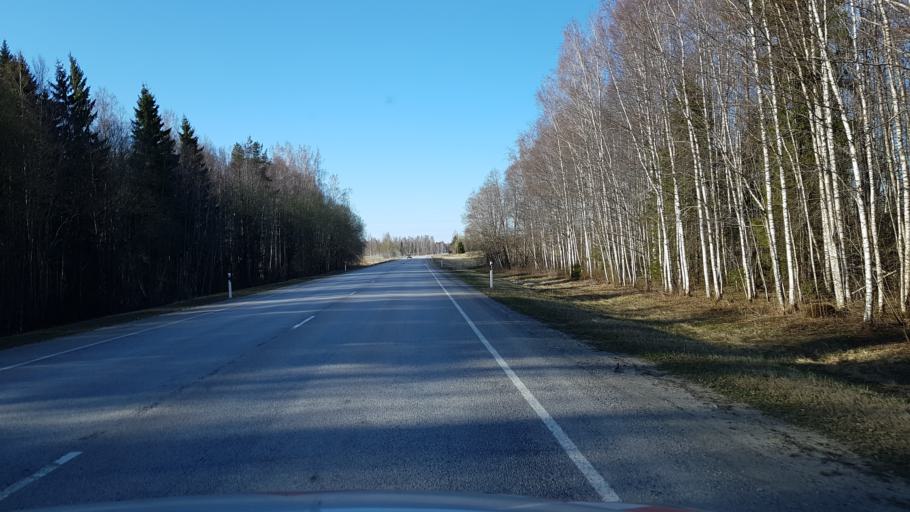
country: EE
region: Ida-Virumaa
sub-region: Johvi vald
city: Johvi
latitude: 59.1813
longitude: 27.3484
